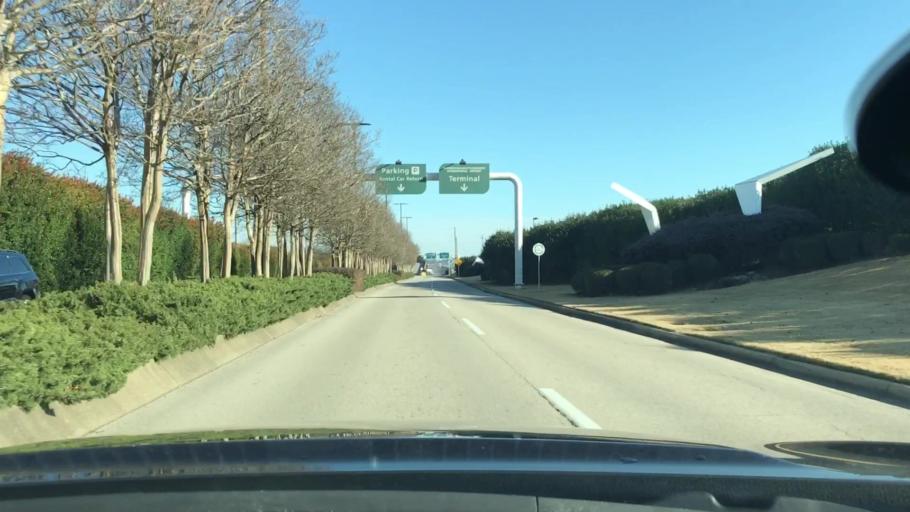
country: US
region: Alabama
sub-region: Jefferson County
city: Tarrant
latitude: 33.5565
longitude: -86.7512
